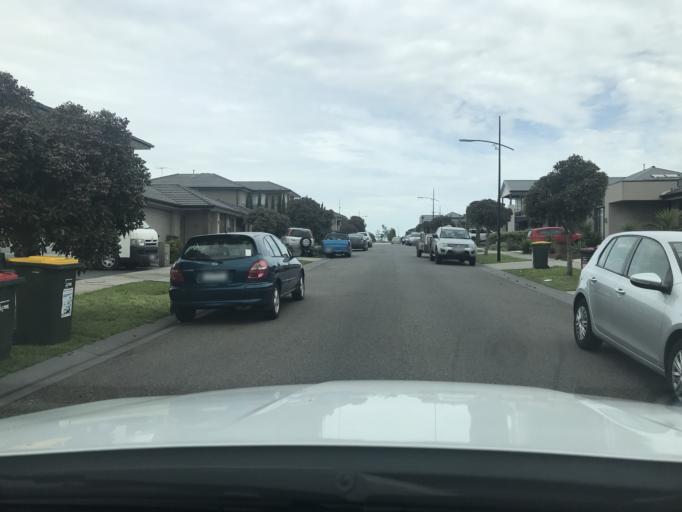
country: AU
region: Victoria
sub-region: Hume
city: Roxburgh Park
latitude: -37.5999
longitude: 144.9029
